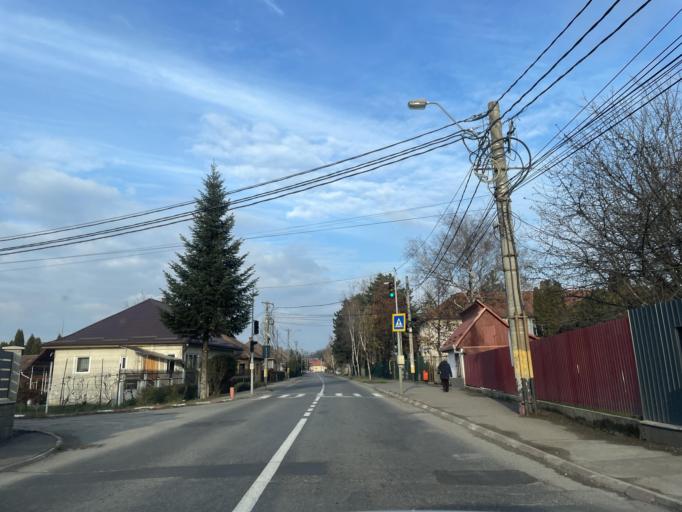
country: RO
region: Mures
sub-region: Municipiul Reghin
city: Reghin
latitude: 46.7749
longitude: 24.7074
